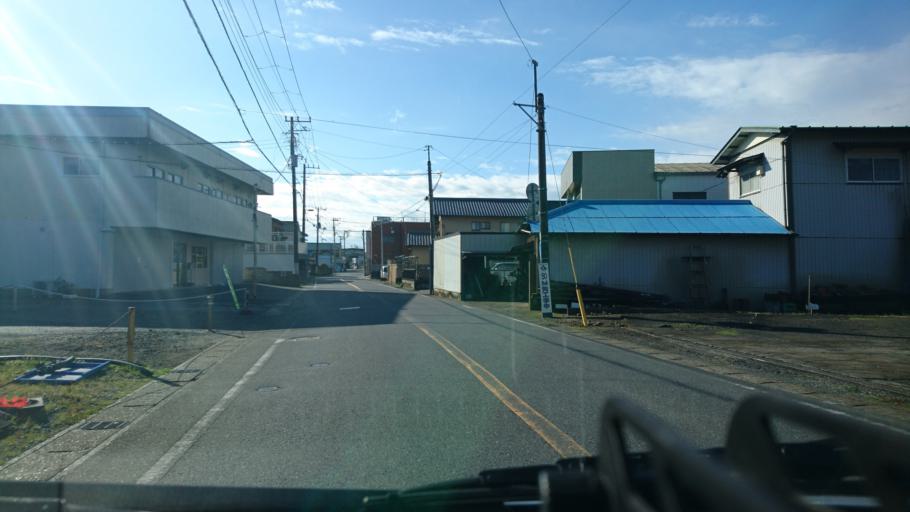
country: JP
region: Chiba
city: Kisarazu
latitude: 35.3767
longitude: 139.9221
